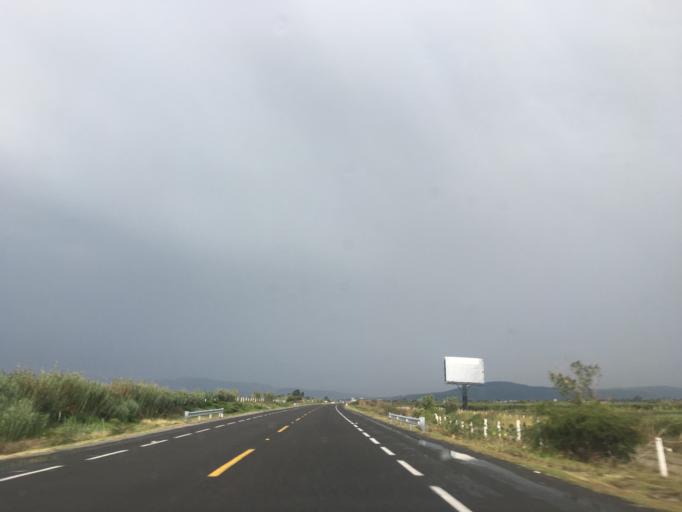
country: MX
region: Michoacan
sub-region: Alvaro Obregon
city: Lazaro Cardenas (La Purisima)
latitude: 19.8668
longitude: -101.0078
